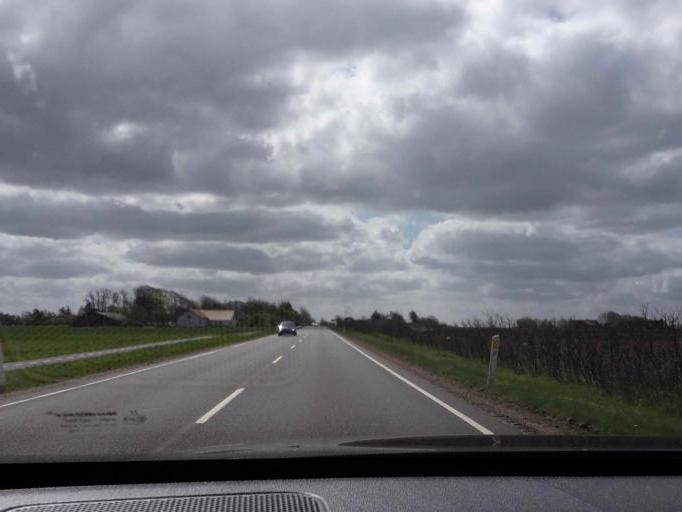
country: DK
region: South Denmark
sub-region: Varde Kommune
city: Olgod
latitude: 55.7524
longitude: 8.6198
